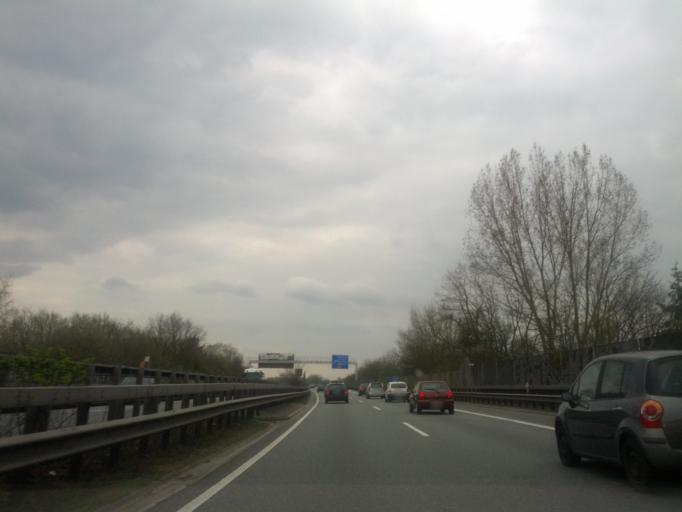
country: DE
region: Lower Saxony
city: Oldenburg
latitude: 53.1398
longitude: 8.1903
